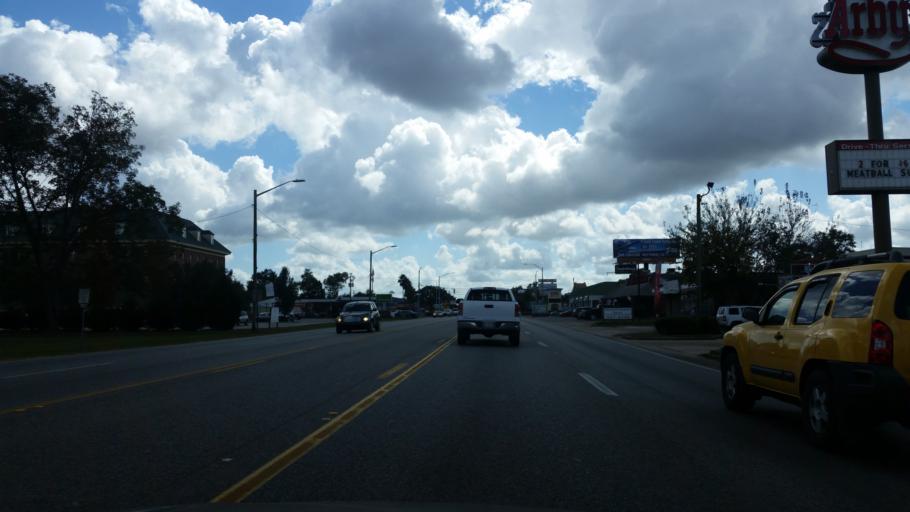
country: US
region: Alabama
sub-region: Baldwin County
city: Robertsdale
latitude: 30.5474
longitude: -87.7084
